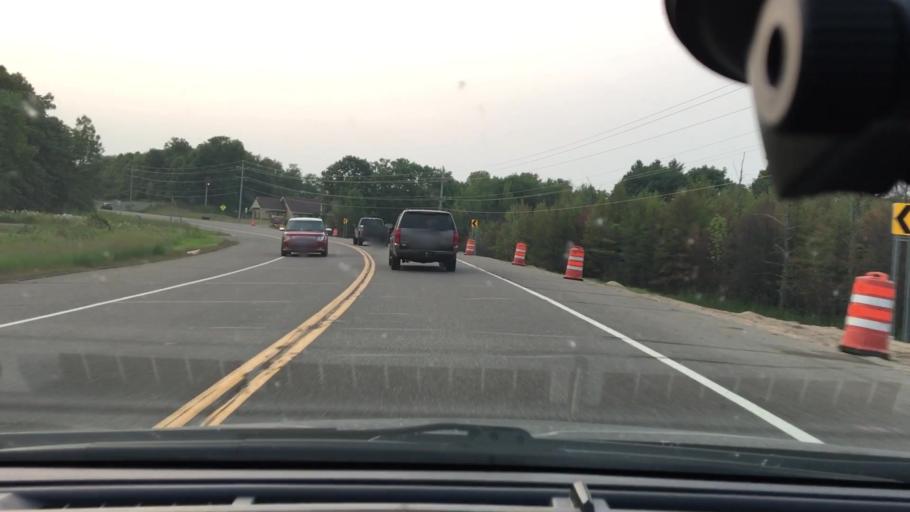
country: US
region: Minnesota
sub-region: Crow Wing County
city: Crosby
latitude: 46.4857
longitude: -93.8985
